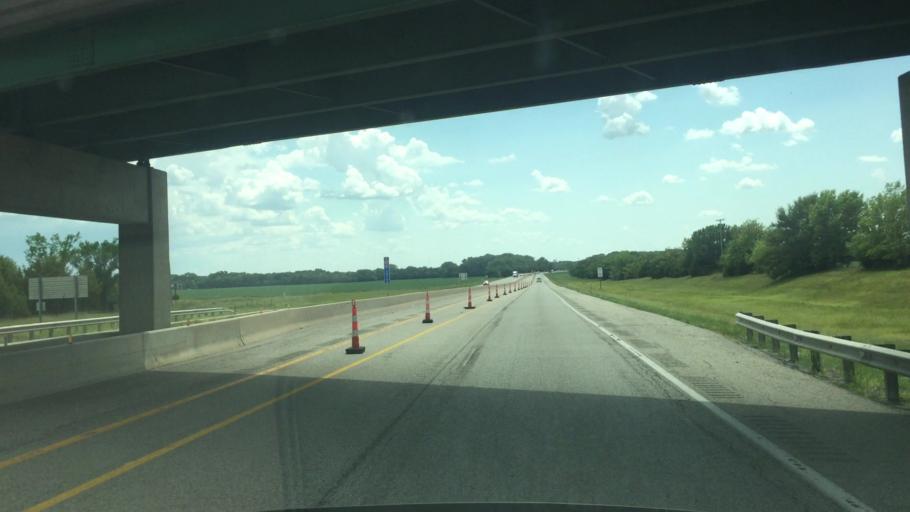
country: US
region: Kansas
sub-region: Lyon County
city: Emporia
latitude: 38.4644
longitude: -96.1901
